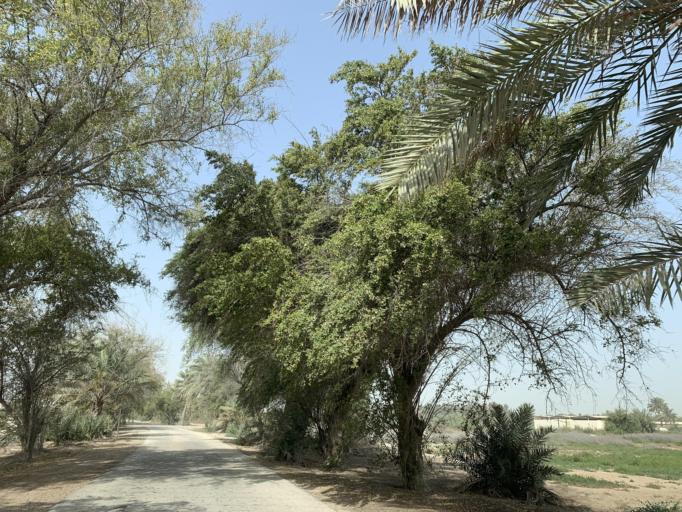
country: BH
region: Northern
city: Madinat `Isa
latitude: 26.1639
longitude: 50.5352
